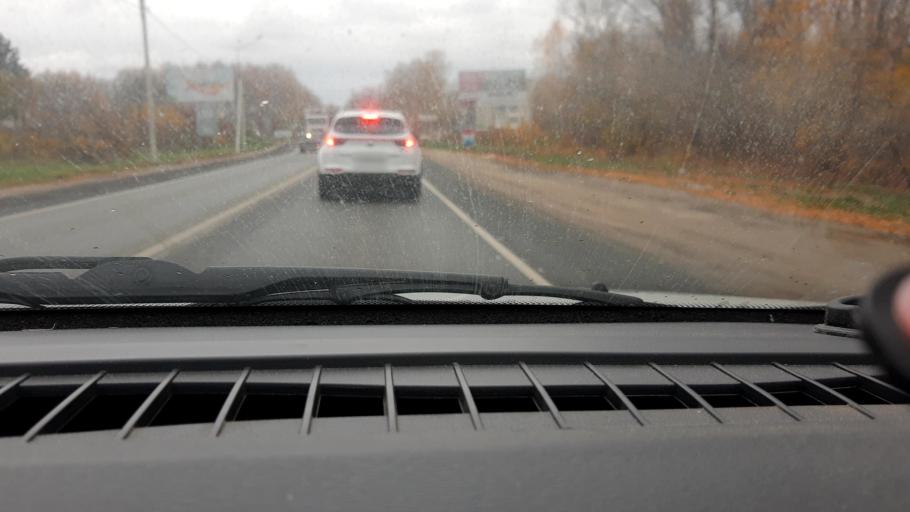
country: RU
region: Nizjnij Novgorod
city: Neklyudovo
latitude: 56.3962
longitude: 44.0092
